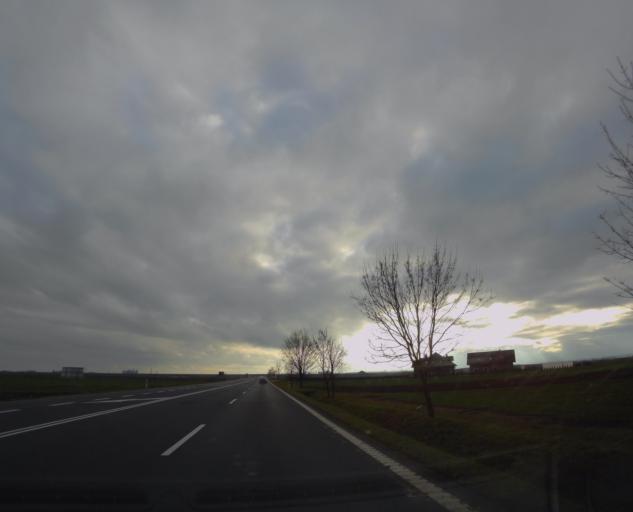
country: PL
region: Subcarpathian Voivodeship
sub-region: Powiat jaroslawski
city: Radymno
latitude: 49.9194
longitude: 22.8201
